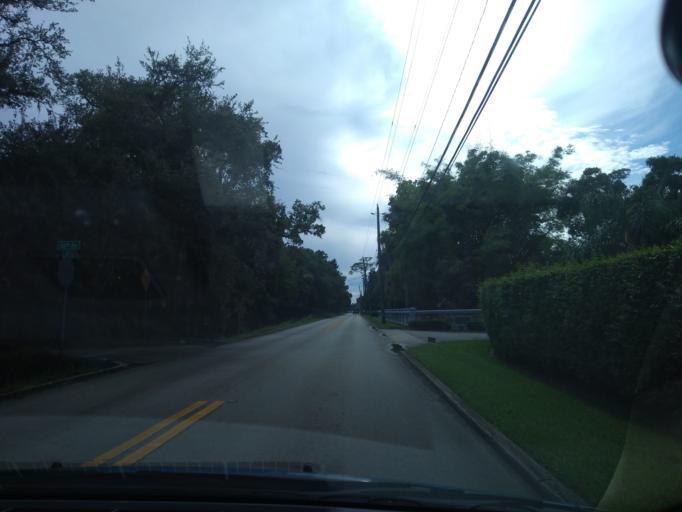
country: US
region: Florida
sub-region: Indian River County
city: Vero Beach South
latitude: 27.6314
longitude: -80.4332
